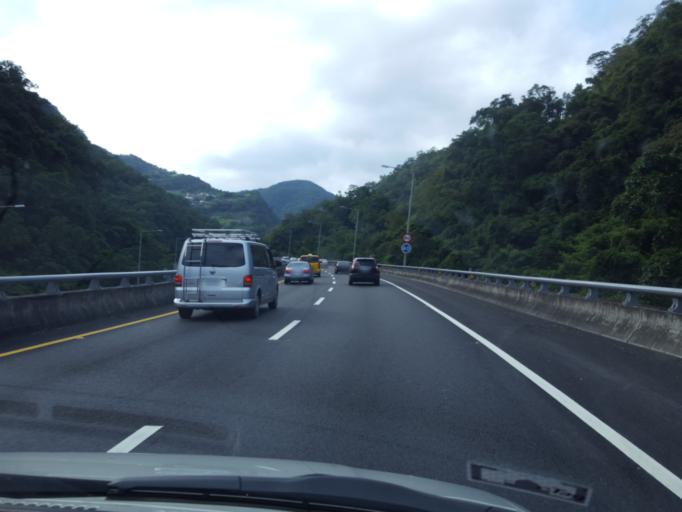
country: TW
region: Taiwan
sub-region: Keelung
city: Keelung
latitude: 24.9455
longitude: 121.7099
